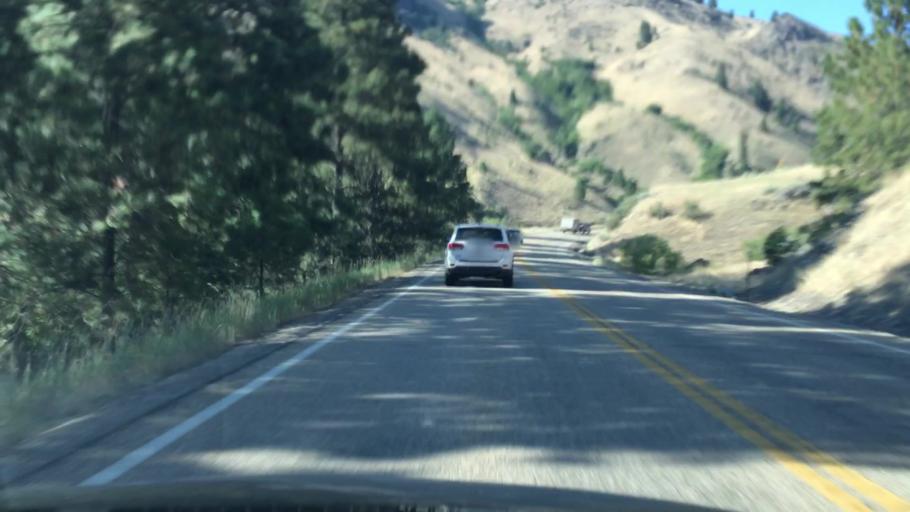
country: US
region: Idaho
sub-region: Boise County
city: Idaho City
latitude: 44.0192
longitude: -116.1517
